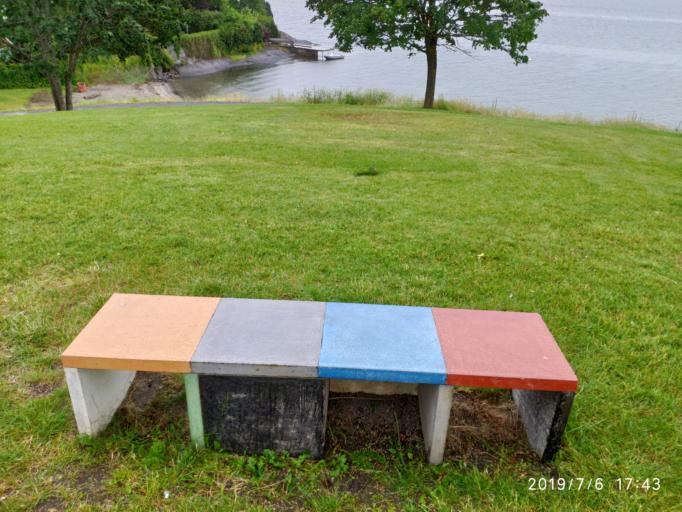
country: NO
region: Akershus
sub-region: Baerum
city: Sandvika
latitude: 59.8884
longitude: 10.5522
